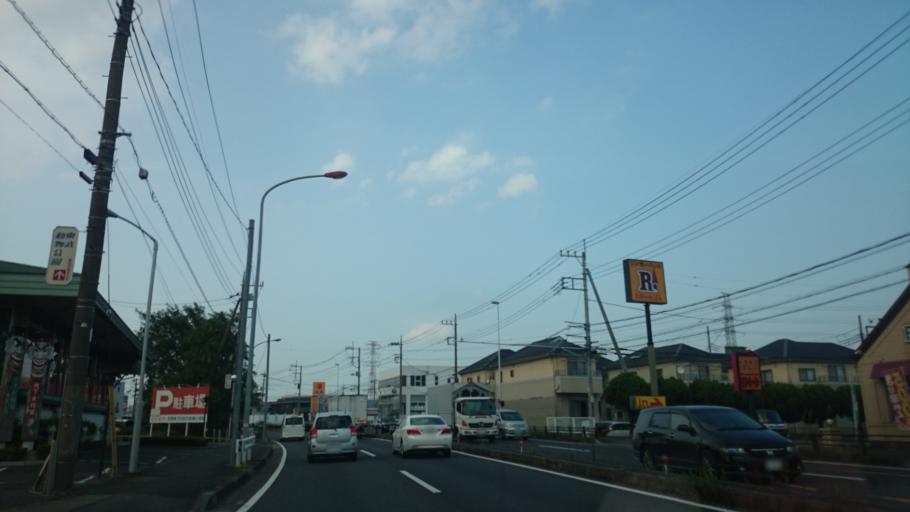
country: JP
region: Saitama
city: Kasukabe
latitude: 35.9700
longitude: 139.7362
